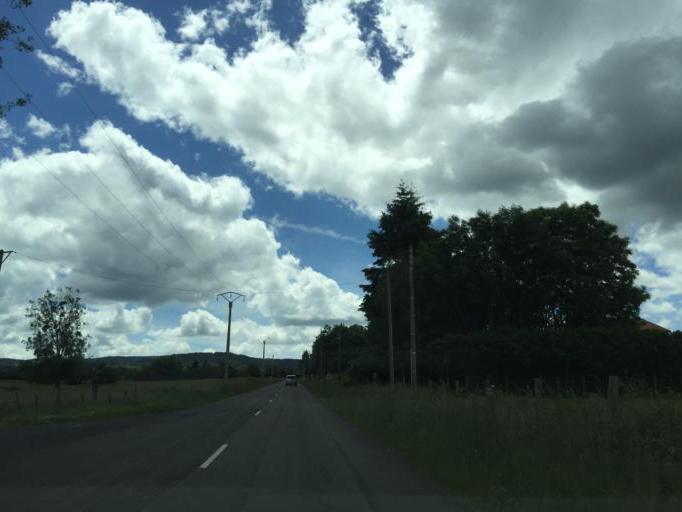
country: FR
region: Rhone-Alpes
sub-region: Departement de la Loire
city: Lezigneux
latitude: 45.5212
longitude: 4.0497
